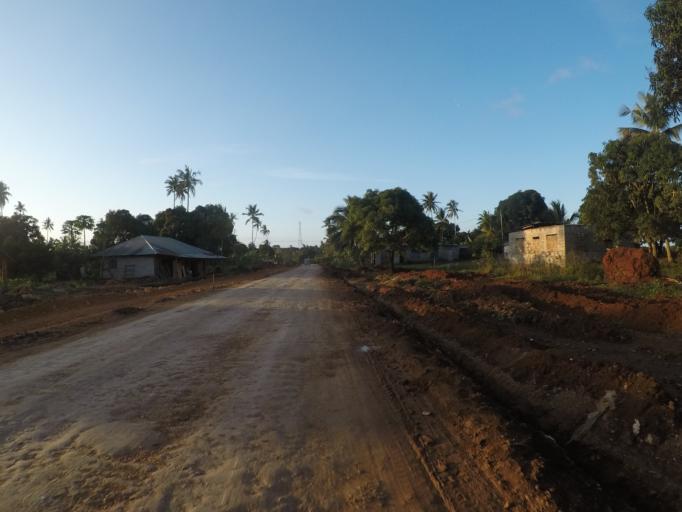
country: TZ
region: Zanzibar North
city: Gamba
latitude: -5.9225
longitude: 39.2999
